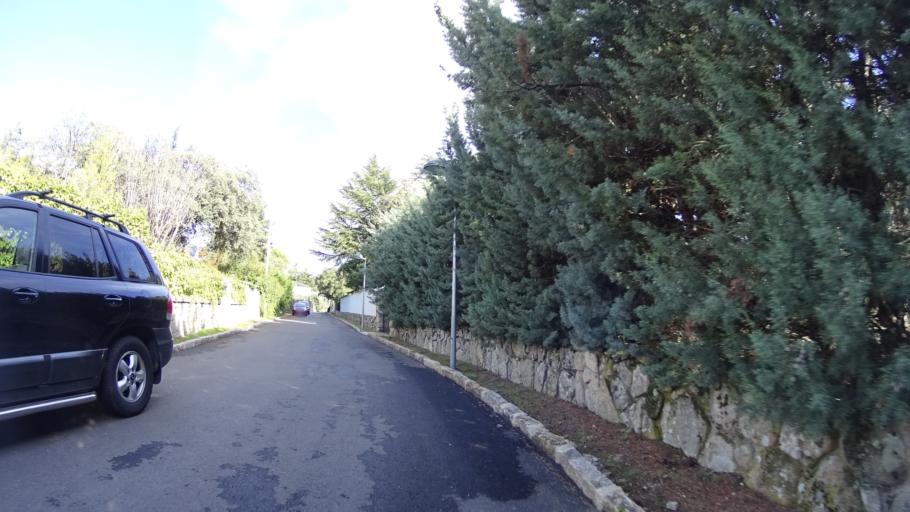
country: ES
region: Madrid
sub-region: Provincia de Madrid
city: Colmenarejo
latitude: 40.5800
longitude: -4.0255
